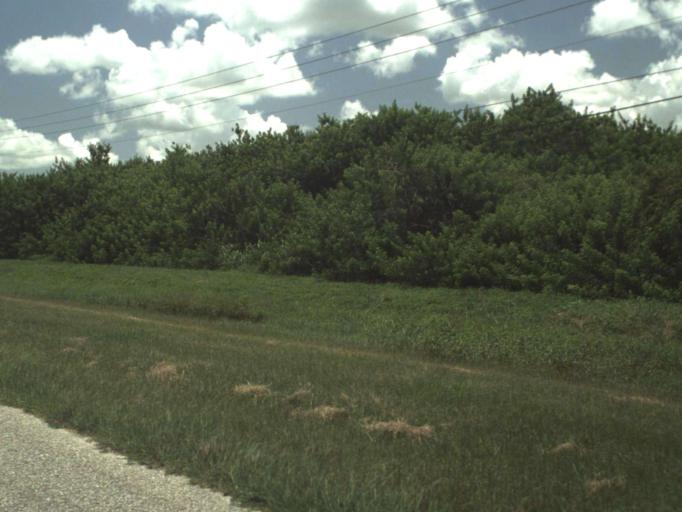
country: US
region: Florida
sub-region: Indian River County
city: Fellsmere
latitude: 27.6403
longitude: -80.6473
